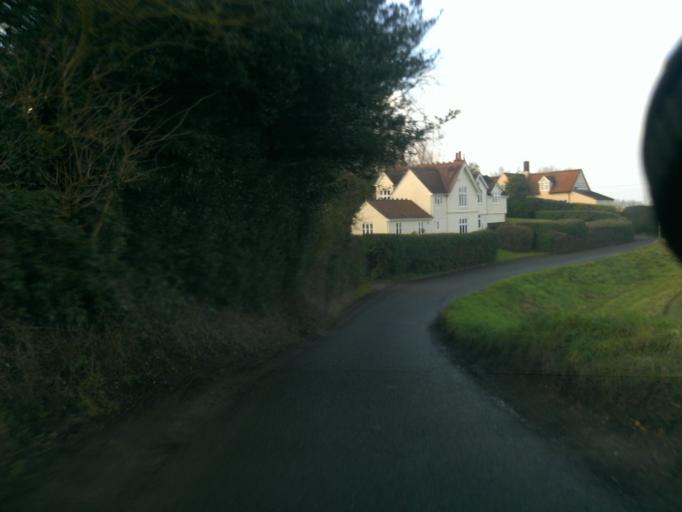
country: GB
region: England
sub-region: Suffolk
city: Sudbury
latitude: 51.9837
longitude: 0.7560
